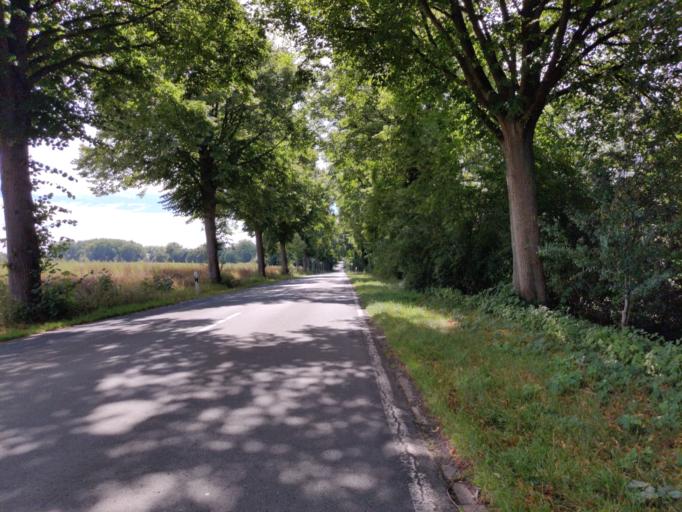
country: DE
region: Lower Saxony
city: Sehlde
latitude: 52.0507
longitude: 10.2828
